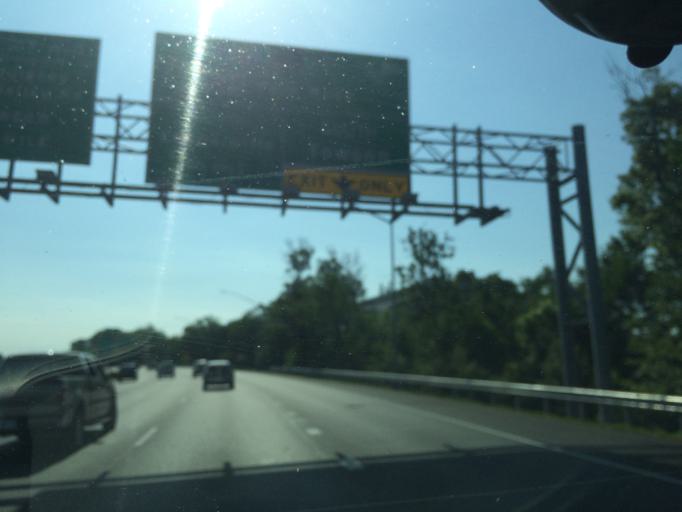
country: US
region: Maryland
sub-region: Baltimore County
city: Lutherville
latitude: 39.4128
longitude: -76.6187
